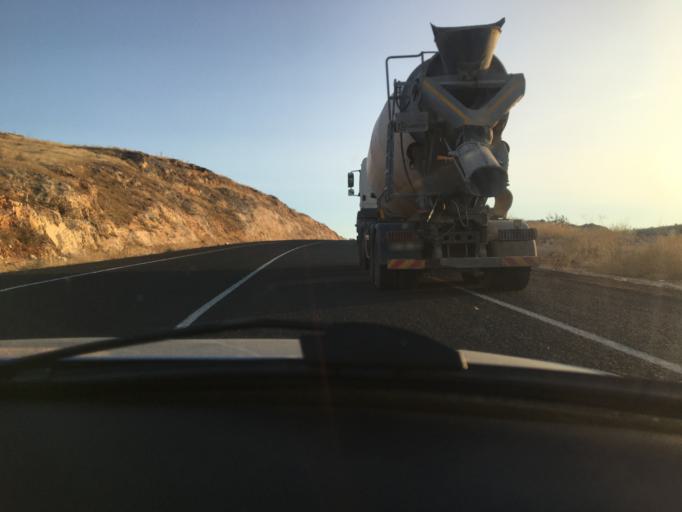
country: TR
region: Sanliurfa
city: Bogurtlen
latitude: 37.1839
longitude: 37.9759
